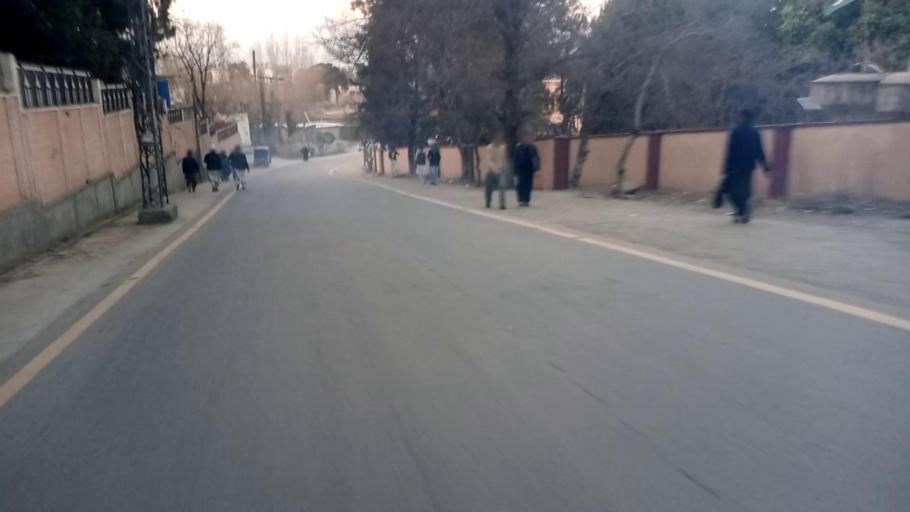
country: PK
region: Khyber Pakhtunkhwa
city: Saidu Sharif
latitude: 34.7572
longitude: 72.3605
